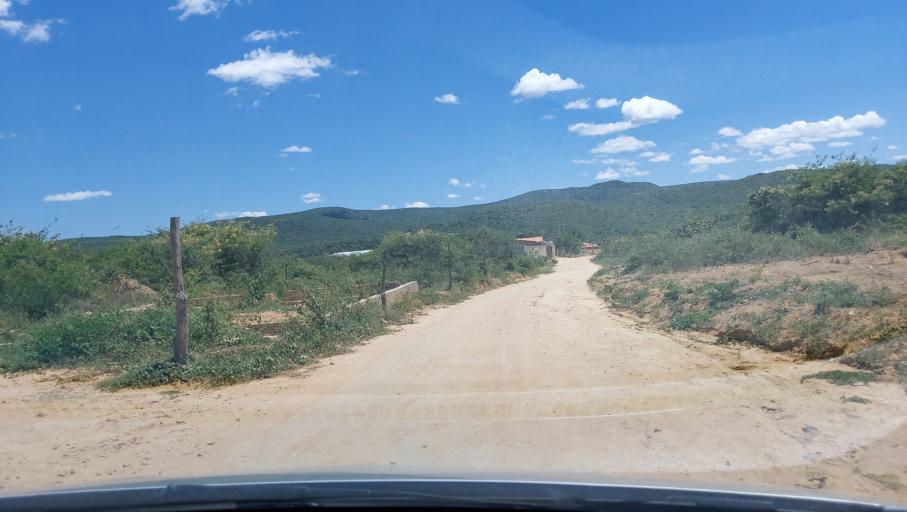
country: BR
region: Bahia
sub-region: Oliveira Dos Brejinhos
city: Beira Rio
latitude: -12.0026
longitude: -42.6320
